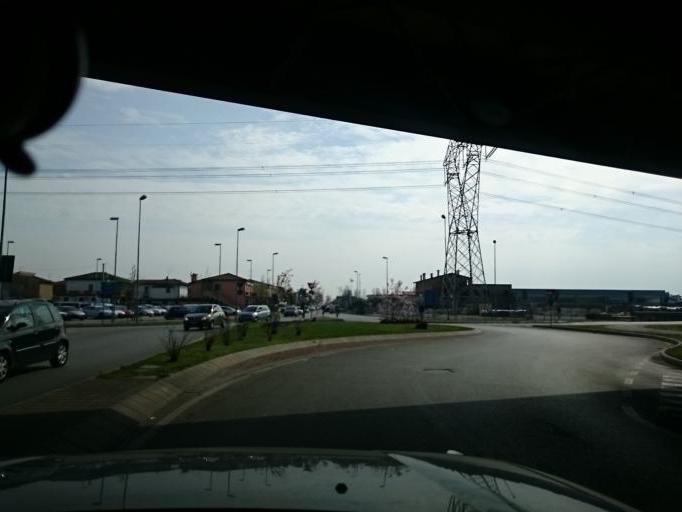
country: IT
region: Veneto
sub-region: Provincia di Padova
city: Mandriola-Sant'Agostino
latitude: 45.3645
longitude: 11.8712
